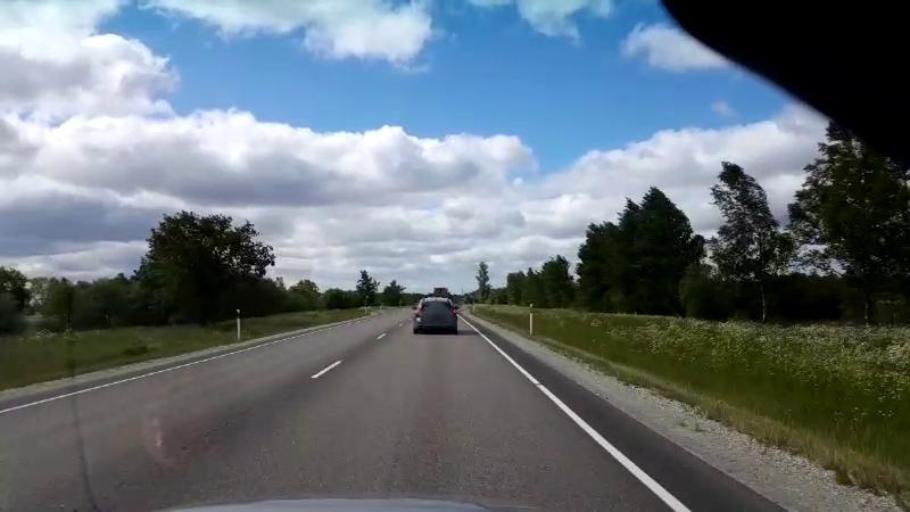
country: EE
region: Paernumaa
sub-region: Sauga vald
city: Sauga
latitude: 58.4915
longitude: 24.5305
